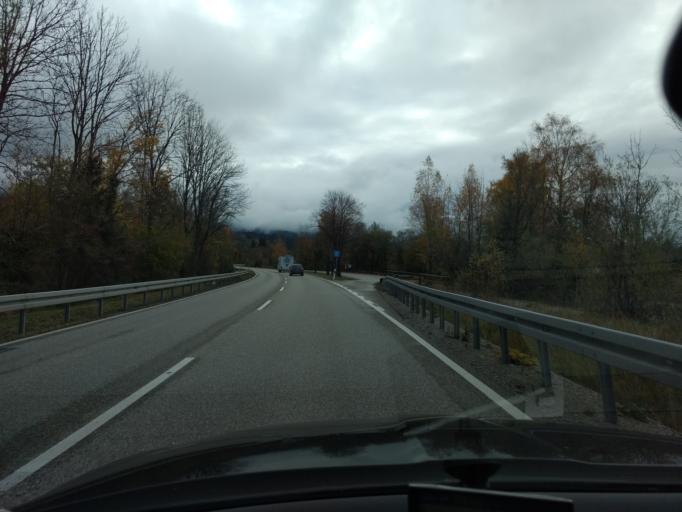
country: DE
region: Bavaria
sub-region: Upper Bavaria
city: Lenggries
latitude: 47.6684
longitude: 11.5776
